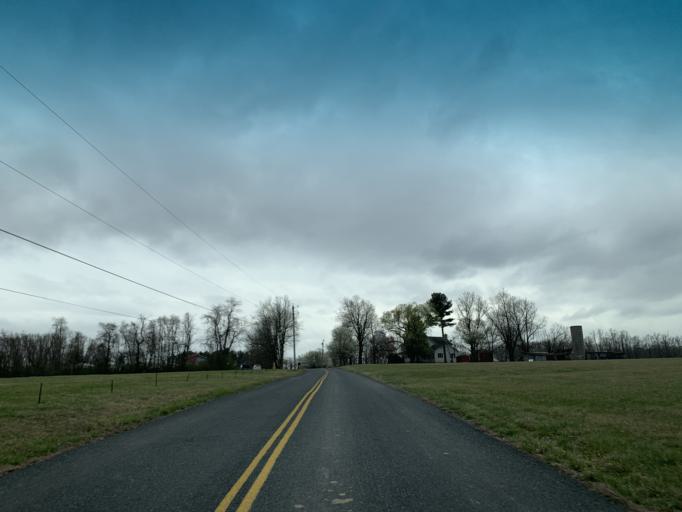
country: US
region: Maryland
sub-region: Harford County
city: Aberdeen
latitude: 39.5275
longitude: -76.2093
